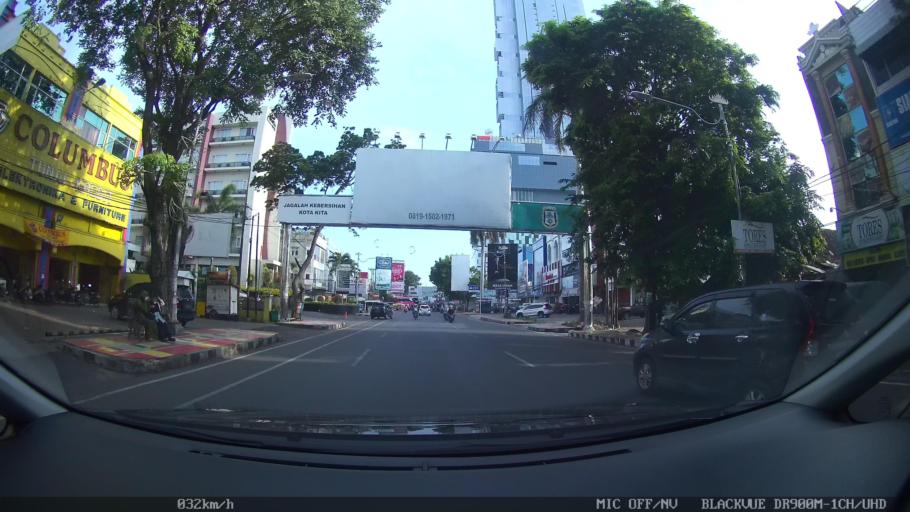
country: ID
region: Lampung
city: Bandarlampung
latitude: -5.4153
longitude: 105.2583
